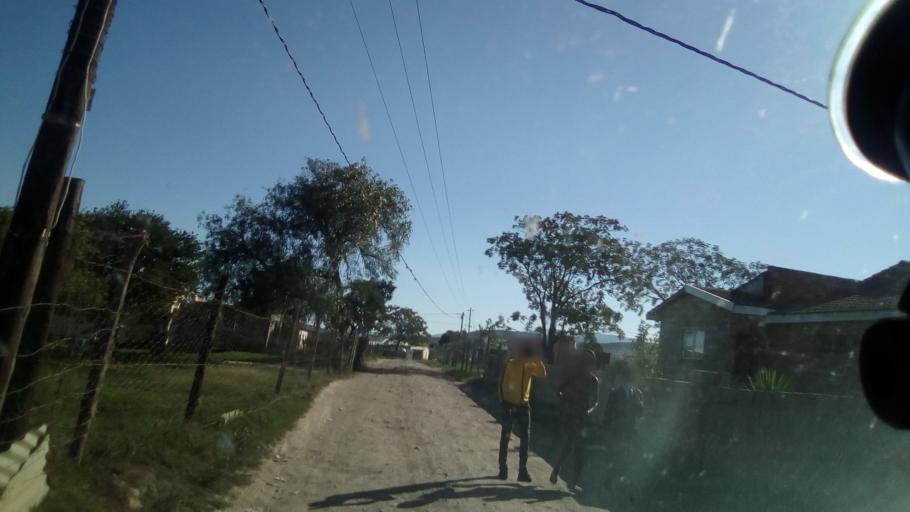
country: ZA
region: Eastern Cape
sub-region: Buffalo City Metropolitan Municipality
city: Bhisho
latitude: -32.8264
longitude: 27.3726
